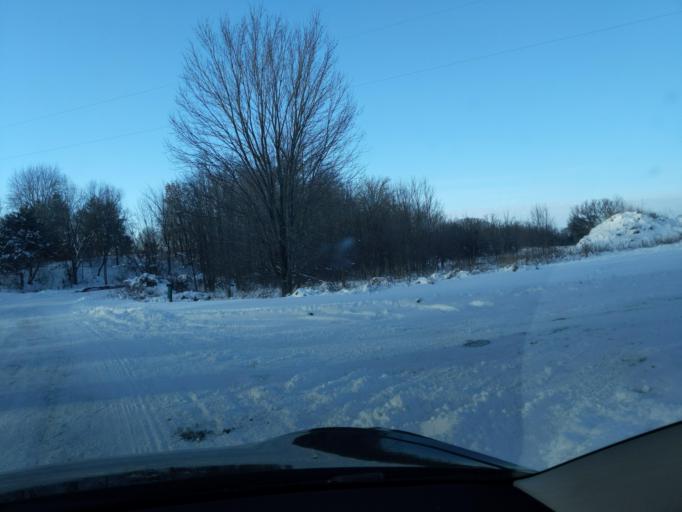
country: US
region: Michigan
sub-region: Ingham County
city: Stockbridge
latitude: 42.4624
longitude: -84.1050
